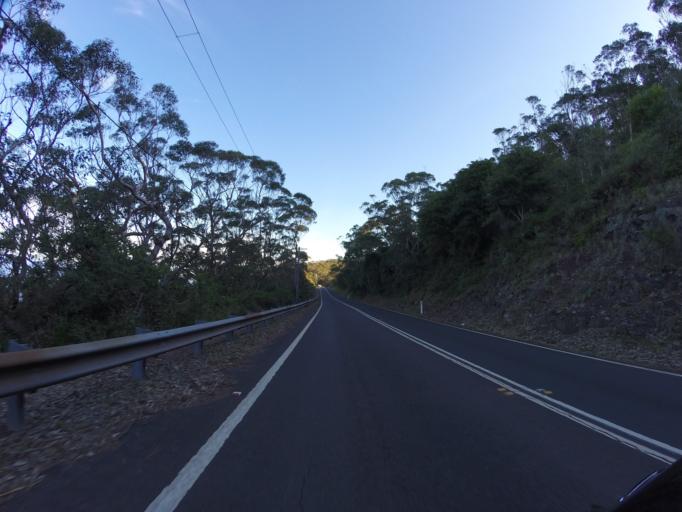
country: AU
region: New South Wales
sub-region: Wollongong
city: Helensburgh
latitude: -34.2123
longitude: 151.0088
